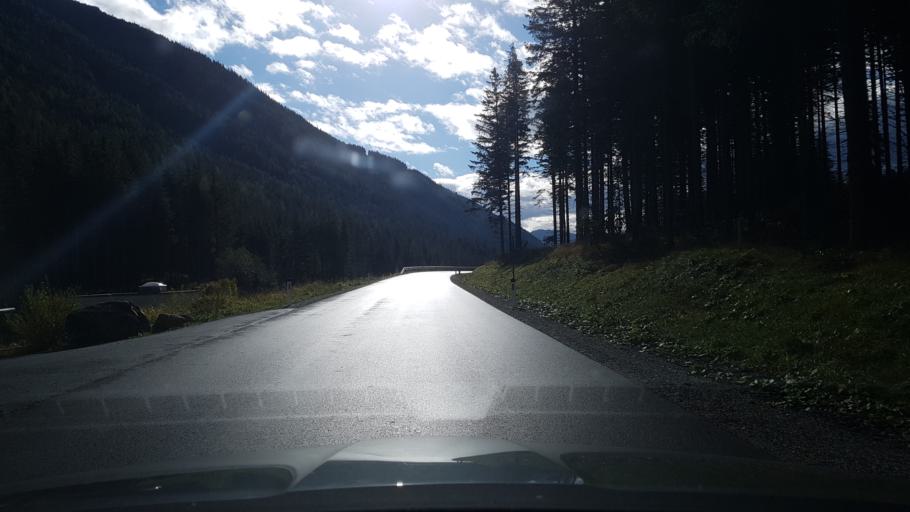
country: AT
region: Styria
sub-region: Politischer Bezirk Murau
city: Schoder
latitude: 47.2300
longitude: 14.0927
